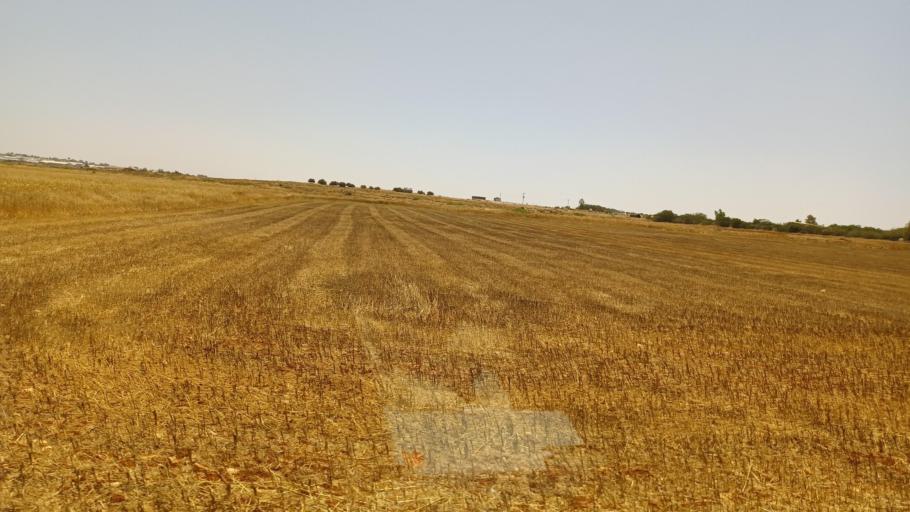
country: CY
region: Ammochostos
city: Liopetri
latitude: 35.0295
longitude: 33.8882
